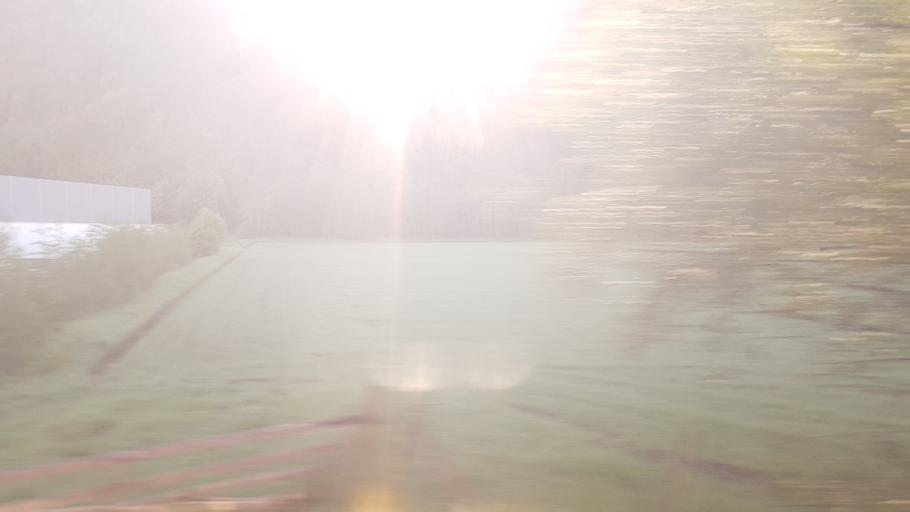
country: NO
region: Sor-Trondelag
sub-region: Melhus
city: Melhus
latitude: 63.2527
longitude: 10.2806
